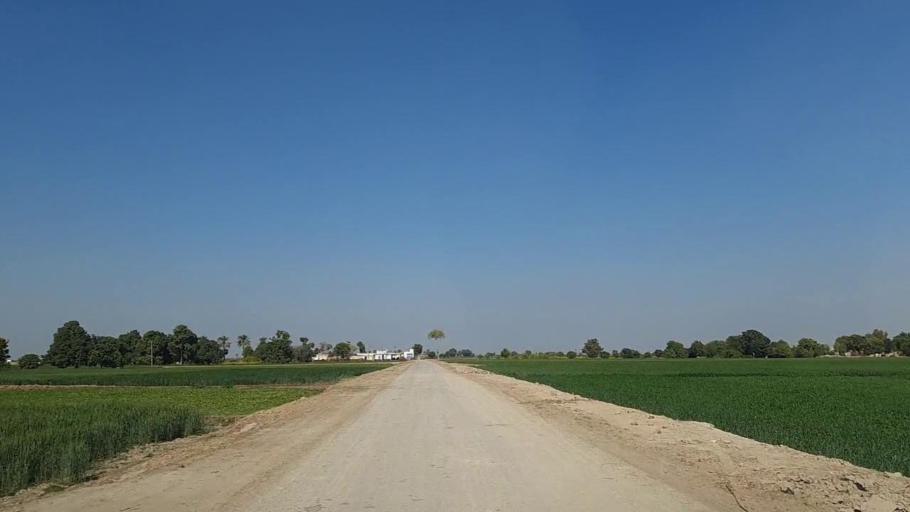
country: PK
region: Sindh
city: Nawabshah
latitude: 26.2567
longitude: 68.4515
